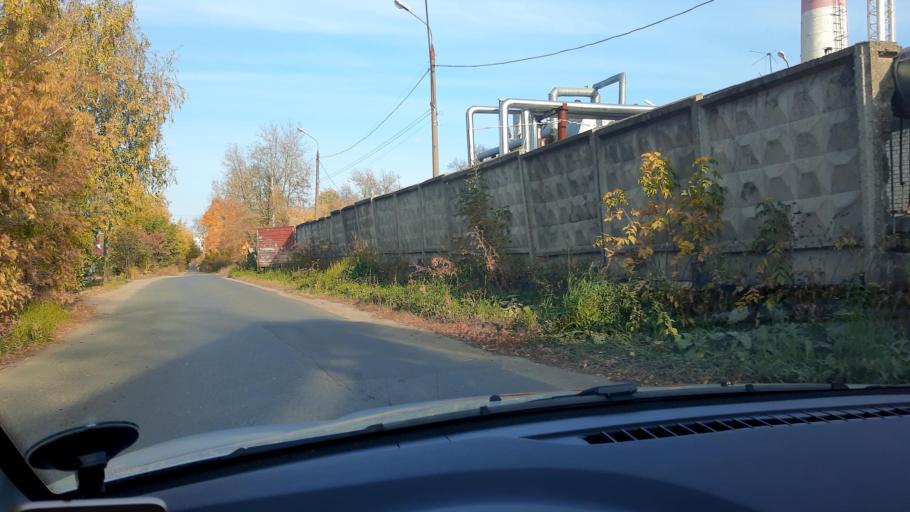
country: RU
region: Nizjnij Novgorod
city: Gorbatovka
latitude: 56.2915
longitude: 43.8537
